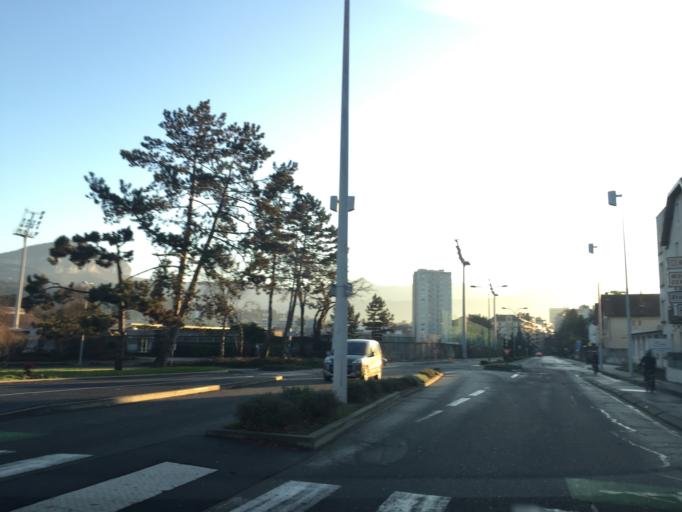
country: FR
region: Rhone-Alpes
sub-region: Departement de la Savoie
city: Cognin
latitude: 45.5733
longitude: 5.9064
